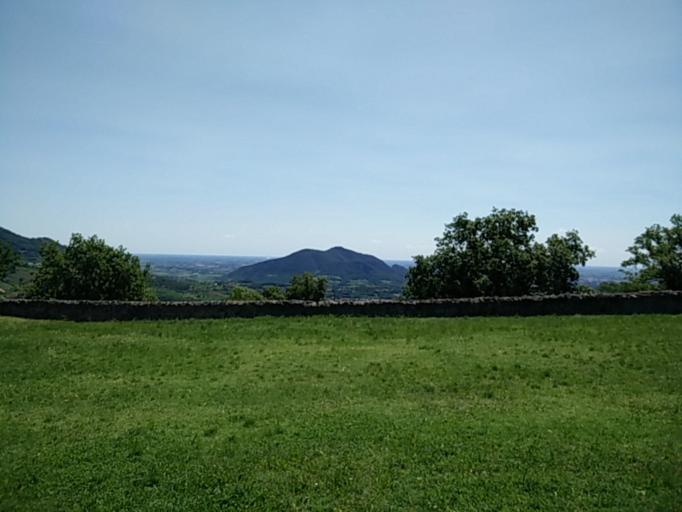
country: IT
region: Veneto
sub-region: Provincia di Padova
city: Fontanafredda
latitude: 45.2767
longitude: 11.6791
